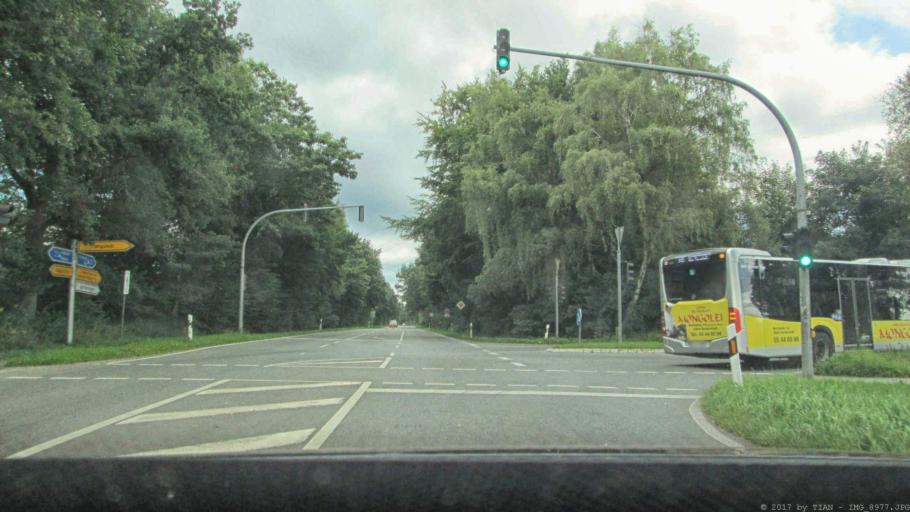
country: DE
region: Schleswig-Holstein
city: Tangstedt
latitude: 53.7268
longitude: 10.0258
